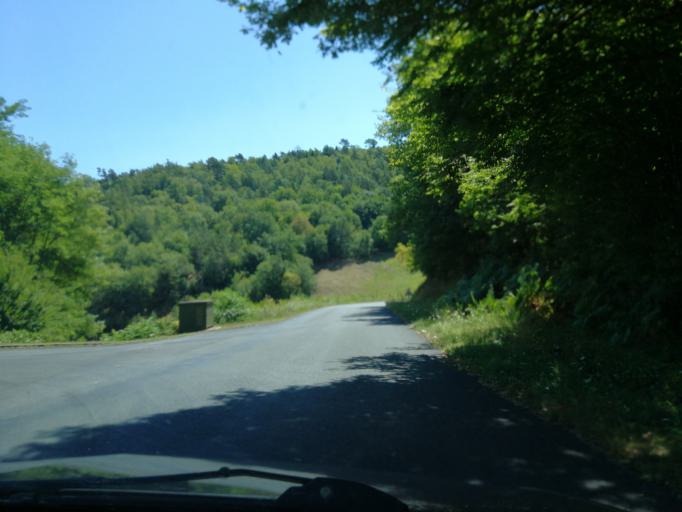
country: FR
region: Limousin
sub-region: Departement de la Correze
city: Argentat
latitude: 45.0910
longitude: 1.9093
